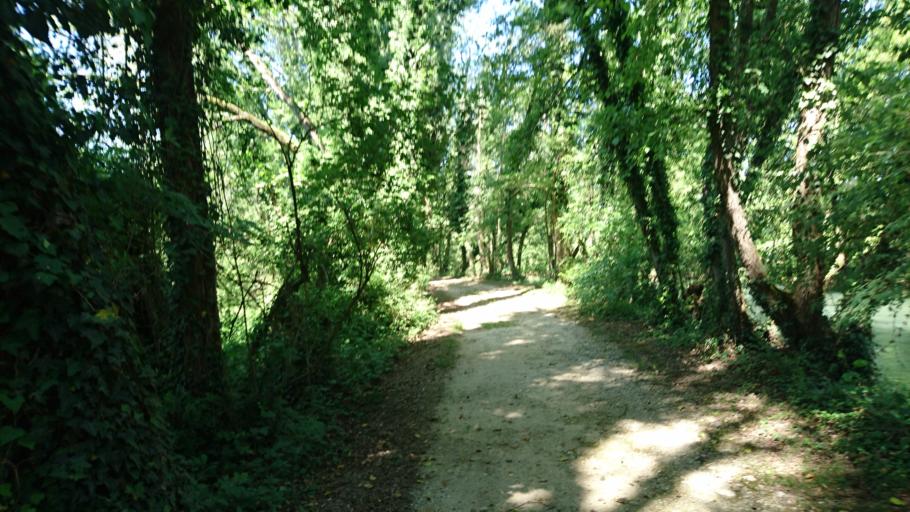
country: IT
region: Veneto
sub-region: Provincia di Treviso
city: Santa Cristina
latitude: 45.6460
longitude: 12.1262
